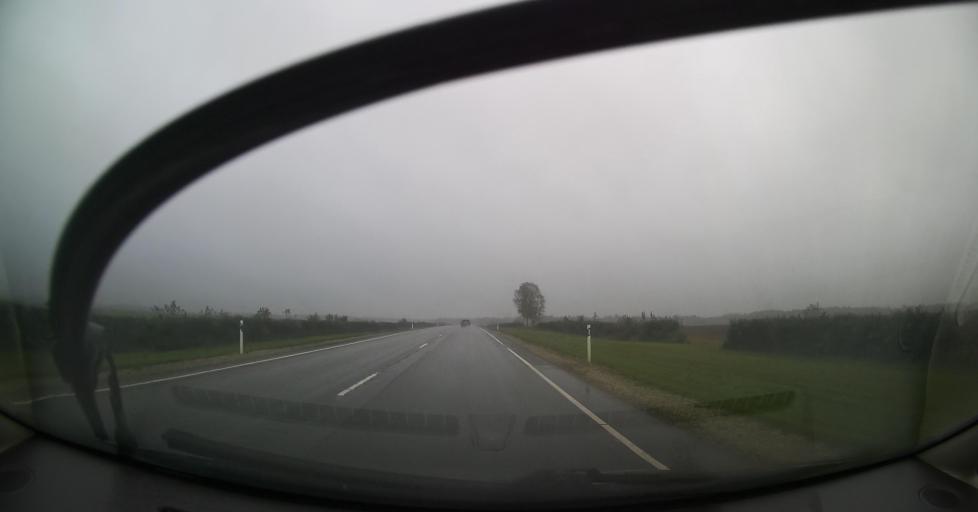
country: EE
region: Jogevamaa
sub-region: Poltsamaa linn
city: Poltsamaa
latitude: 58.6323
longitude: 26.1272
